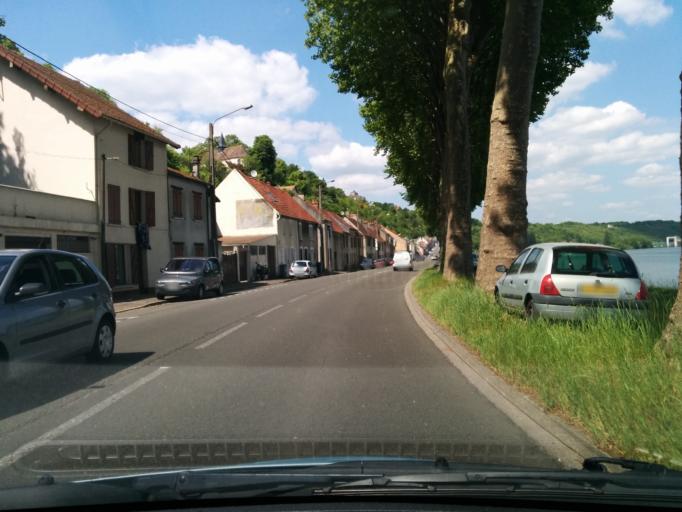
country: FR
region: Ile-de-France
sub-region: Departement des Yvelines
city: Rosny-sur-Seine
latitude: 49.0165
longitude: 1.6107
